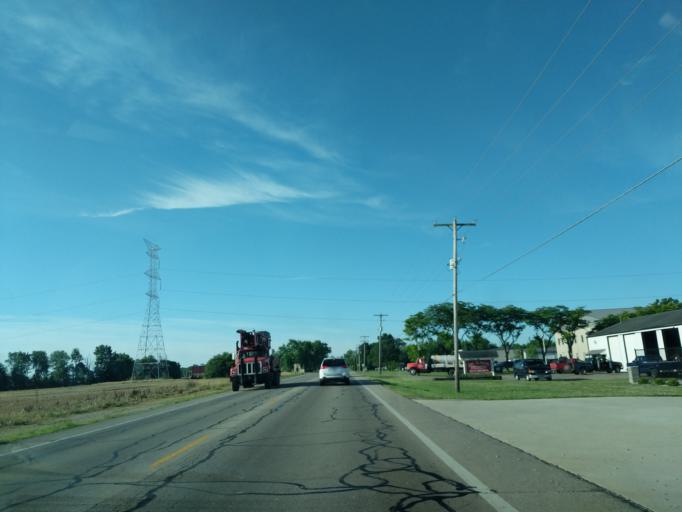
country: US
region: Indiana
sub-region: Hancock County
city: Greenfield
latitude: 39.8647
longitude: -85.7701
